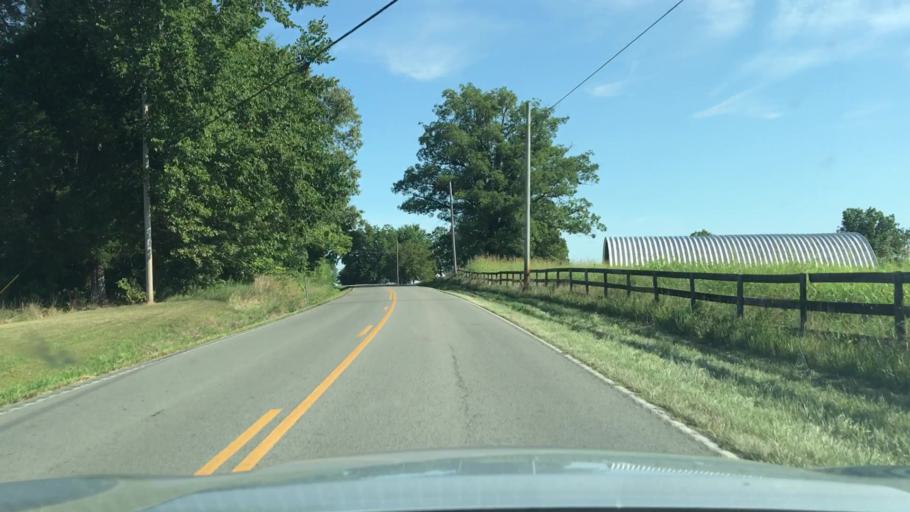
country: US
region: Kentucky
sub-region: Muhlenberg County
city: Greenville
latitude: 37.1599
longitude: -87.1422
